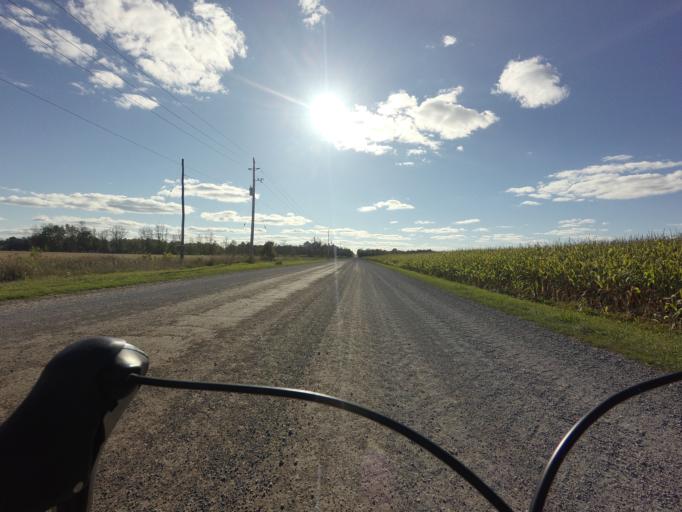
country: CA
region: Ontario
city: Bells Corners
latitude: 45.1160
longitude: -75.7032
